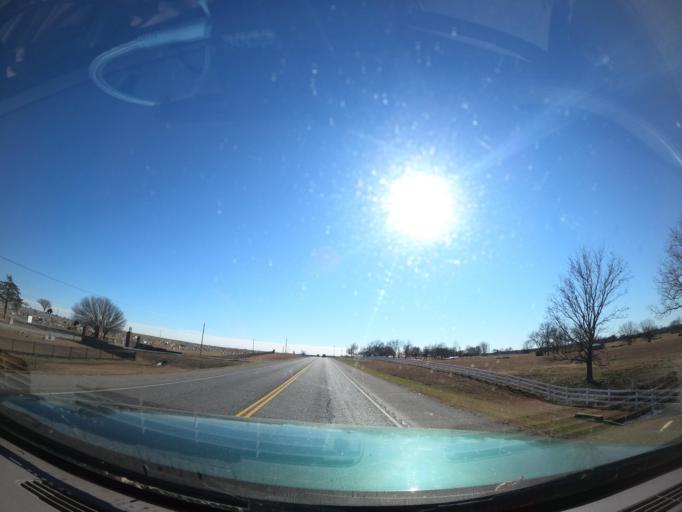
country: US
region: Oklahoma
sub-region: Muskogee County
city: Haskell
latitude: 35.8378
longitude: -95.6777
